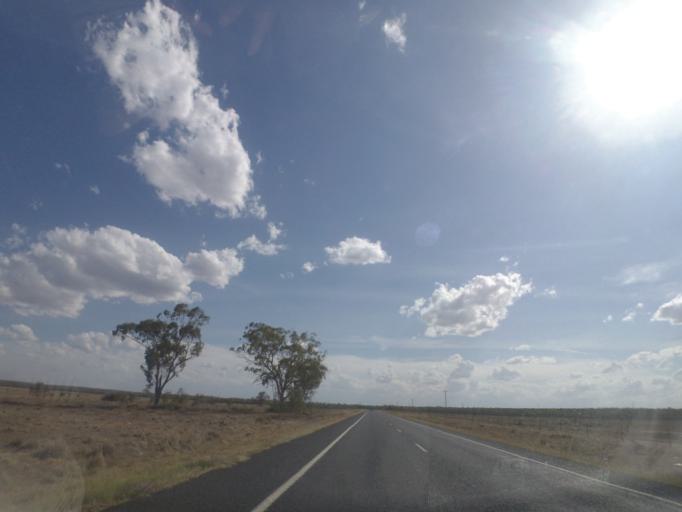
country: AU
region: New South Wales
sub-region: Moree Plains
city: Boggabilla
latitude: -28.5268
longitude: 150.9016
